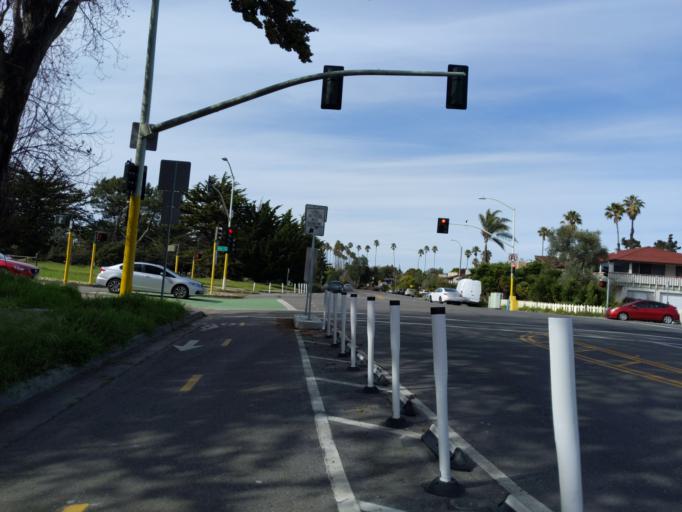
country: US
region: California
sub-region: Alameda County
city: Alameda
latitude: 37.7660
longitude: -122.2715
